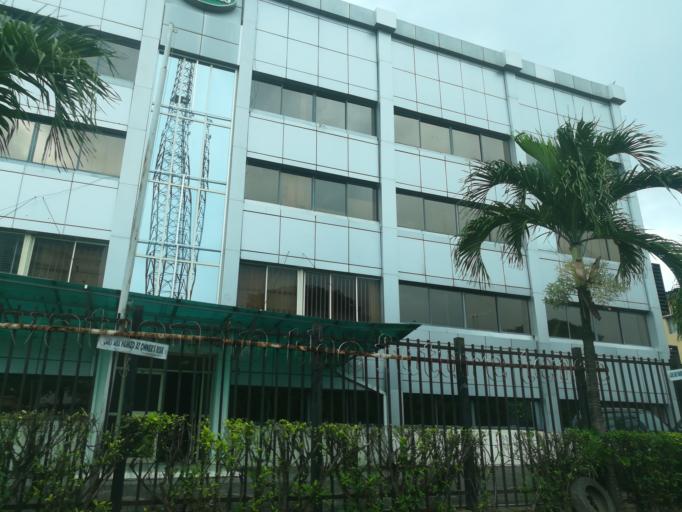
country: NG
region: Lagos
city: Lagos
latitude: 6.4278
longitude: 3.4081
